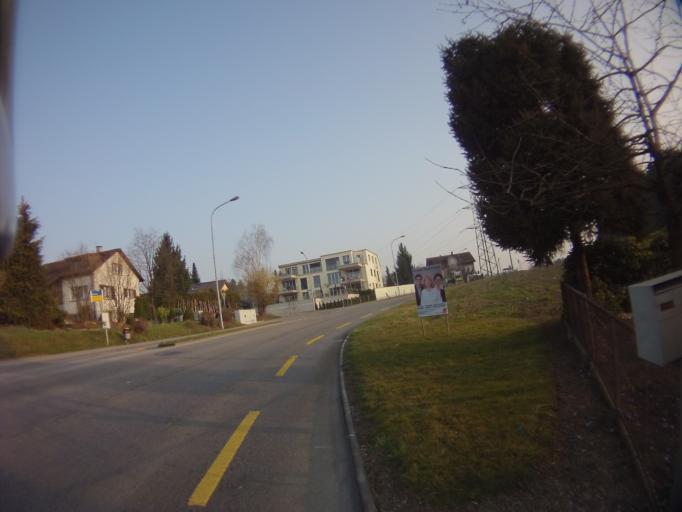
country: CH
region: Zurich
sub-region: Bezirk Affoltern
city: Obfelden / Toussen
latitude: 47.2682
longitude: 8.4331
